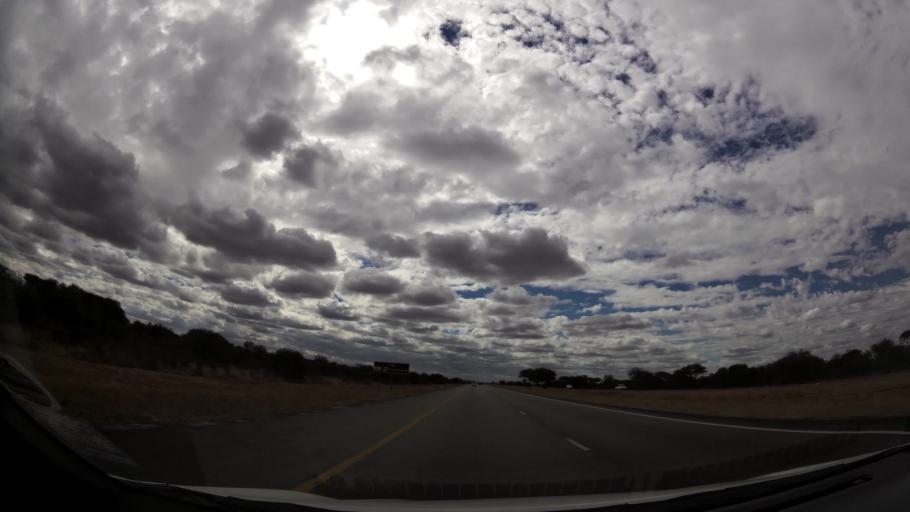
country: ZA
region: Limpopo
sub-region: Waterberg District Municipality
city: Bela-Bela
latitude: -24.9661
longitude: 28.3560
